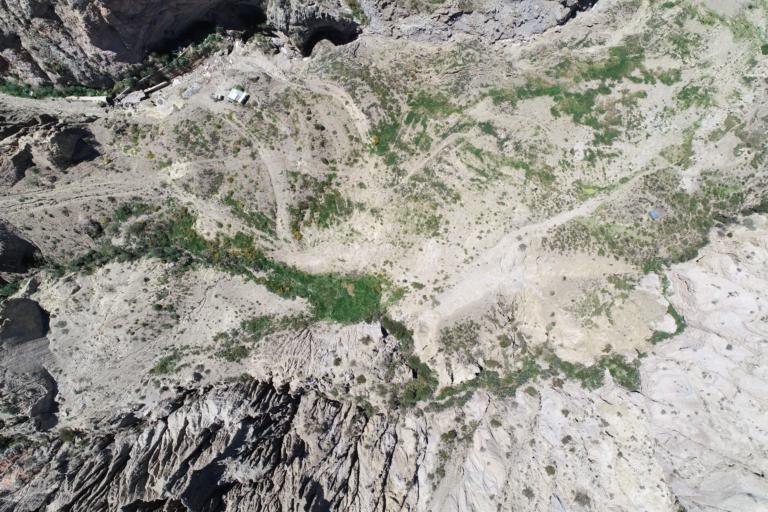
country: BO
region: La Paz
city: La Paz
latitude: -16.5164
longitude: -68.1001
